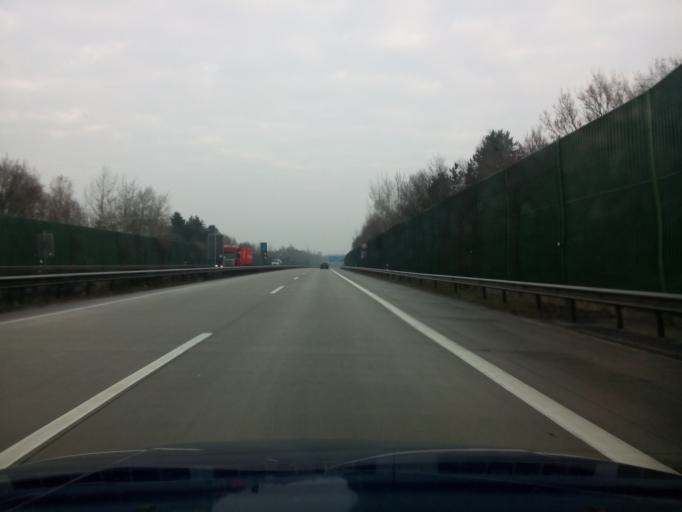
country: DE
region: Lower Saxony
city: Langen
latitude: 53.5709
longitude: 8.6199
